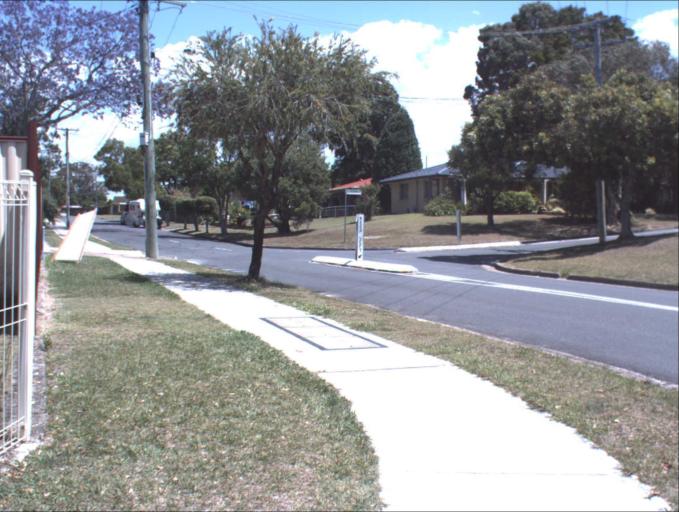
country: AU
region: Queensland
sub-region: Logan
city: Rochedale South
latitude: -27.5901
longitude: 153.1264
